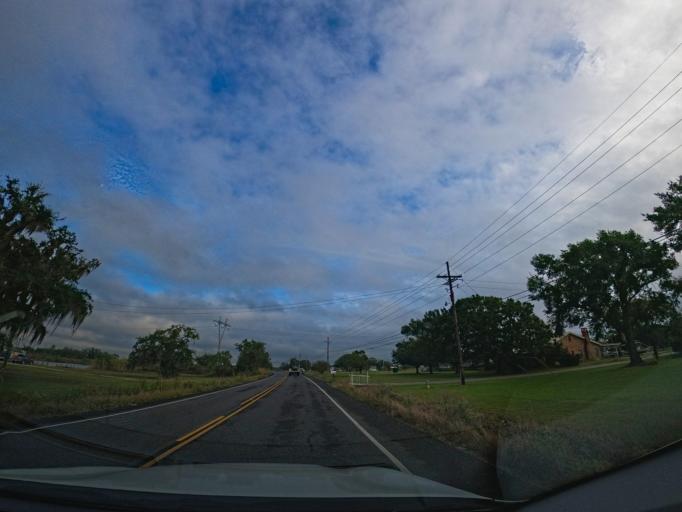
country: US
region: Louisiana
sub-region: Terrebonne Parish
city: Dulac
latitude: 29.4477
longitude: -90.7024
